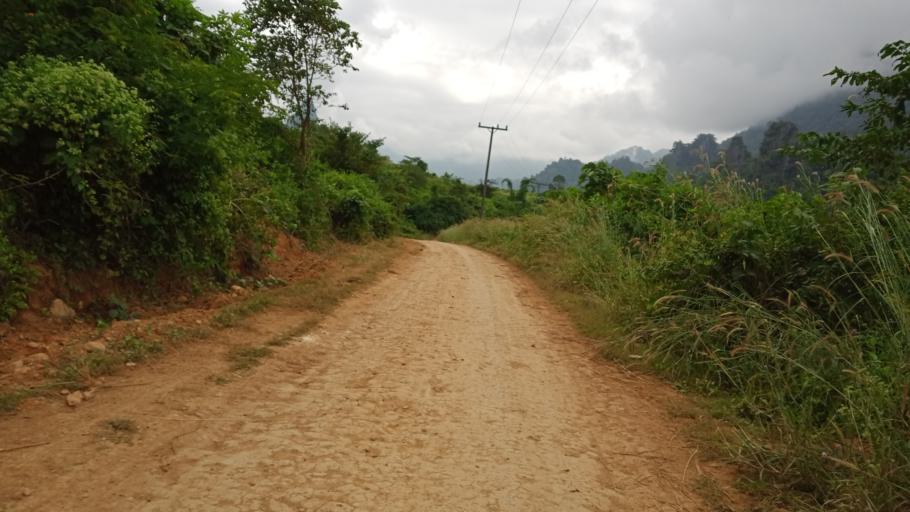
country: LA
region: Xiangkhoang
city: Phonsavan
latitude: 19.0914
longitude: 103.0054
